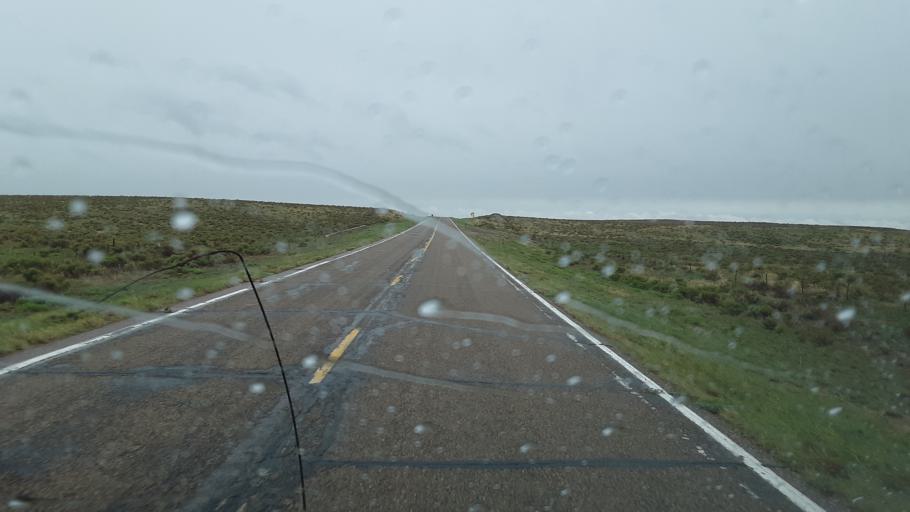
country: US
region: Colorado
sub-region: Lincoln County
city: Hugo
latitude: 38.8546
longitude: -103.1539
